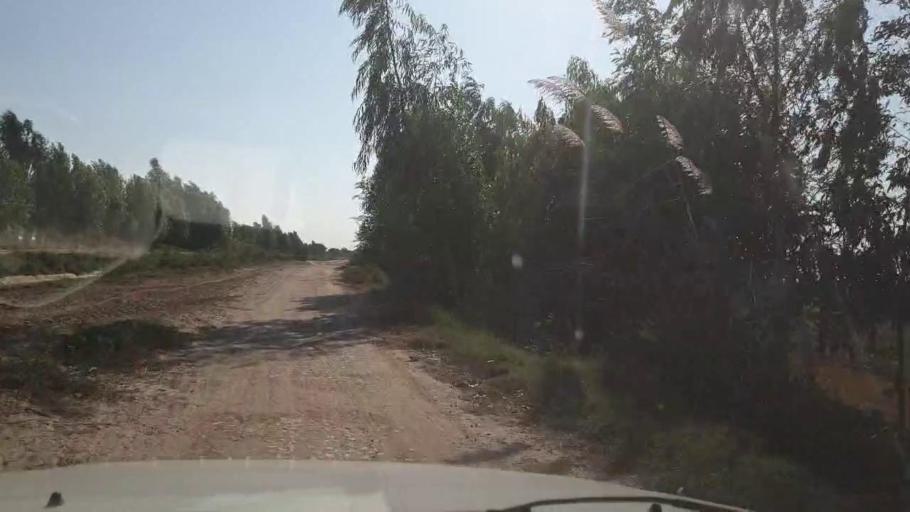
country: PK
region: Sindh
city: Chuhar Jamali
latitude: 24.4835
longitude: 67.8199
